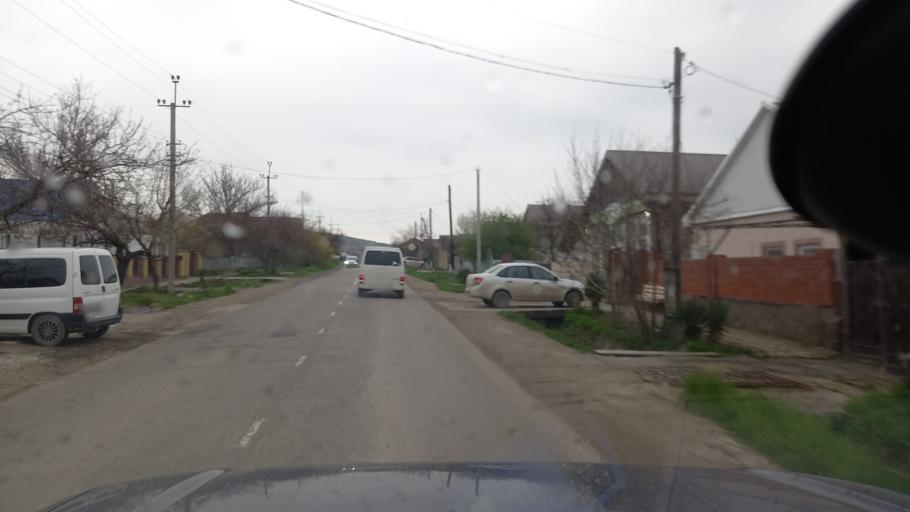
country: RU
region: Krasnodarskiy
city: Sukko
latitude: 44.8583
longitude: 37.4372
